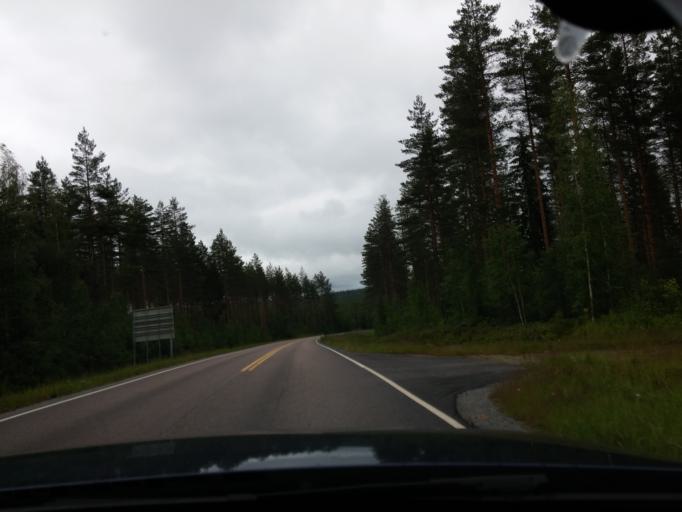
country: FI
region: Central Finland
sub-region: Saarijaervi-Viitasaari
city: Pylkoenmaeki
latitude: 62.5911
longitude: 24.5973
